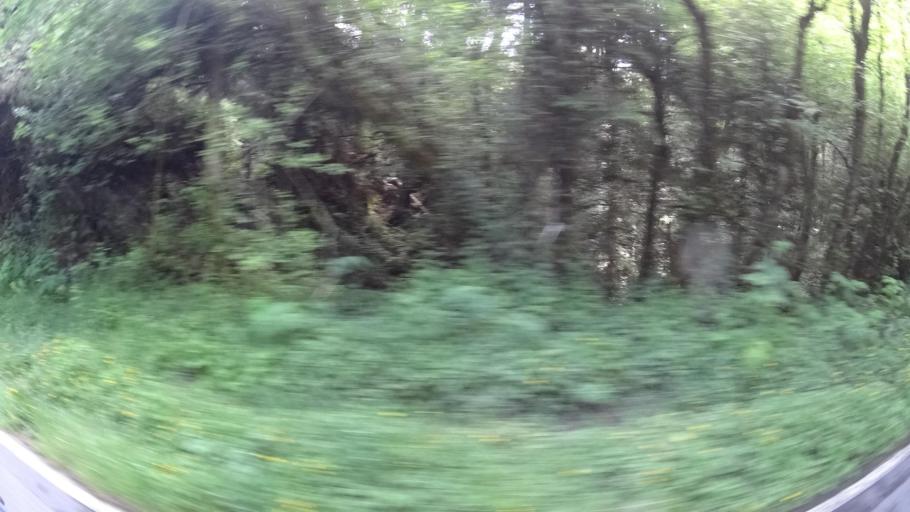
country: US
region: California
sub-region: Humboldt County
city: McKinleyville
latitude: 40.9922
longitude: -124.1118
